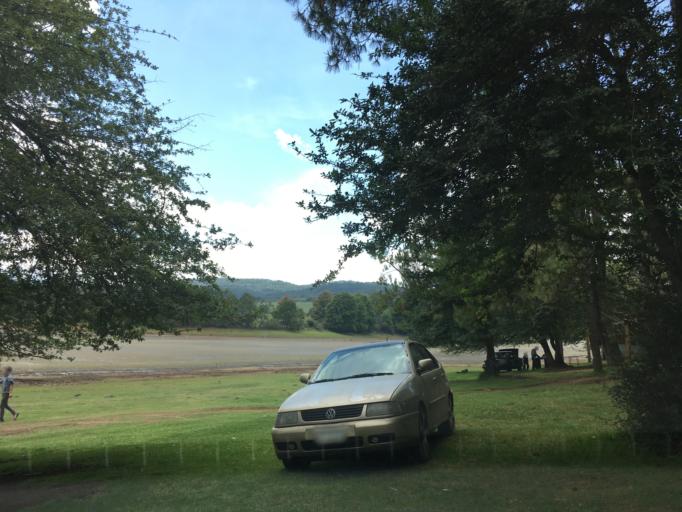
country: MX
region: Michoacan
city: Acuitzio del Canje
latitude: 19.5246
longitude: -101.2450
